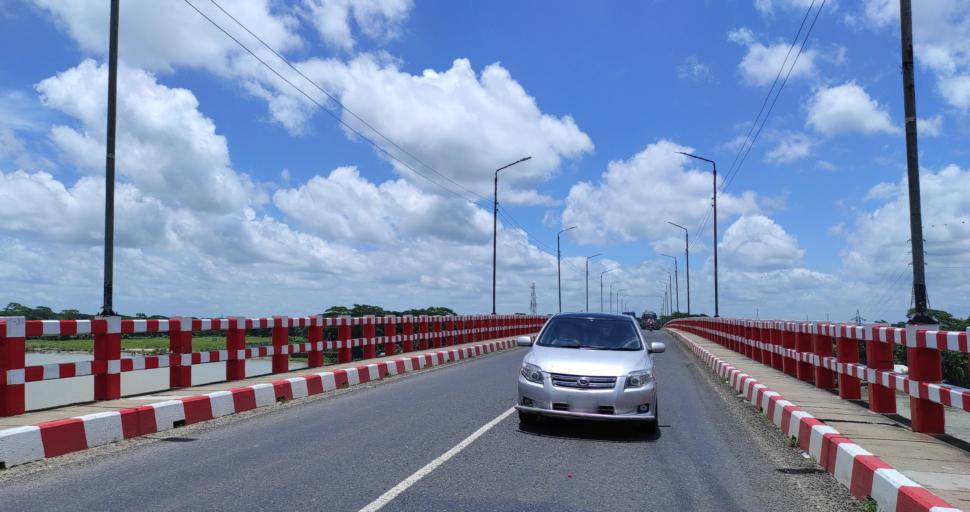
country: BD
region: Barisal
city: Gaurnadi
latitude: 22.8247
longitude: 90.2627
